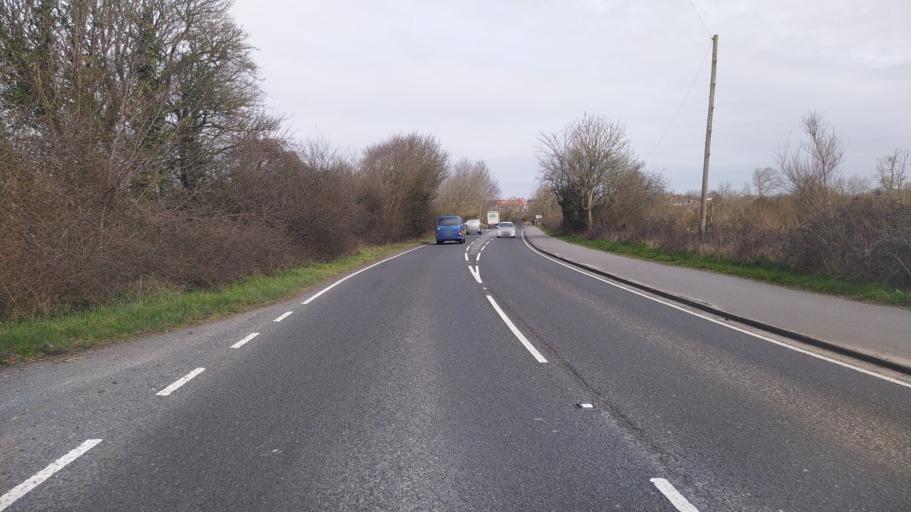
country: GB
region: England
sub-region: Dorset
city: Dorchester
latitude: 50.7275
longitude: -2.4609
